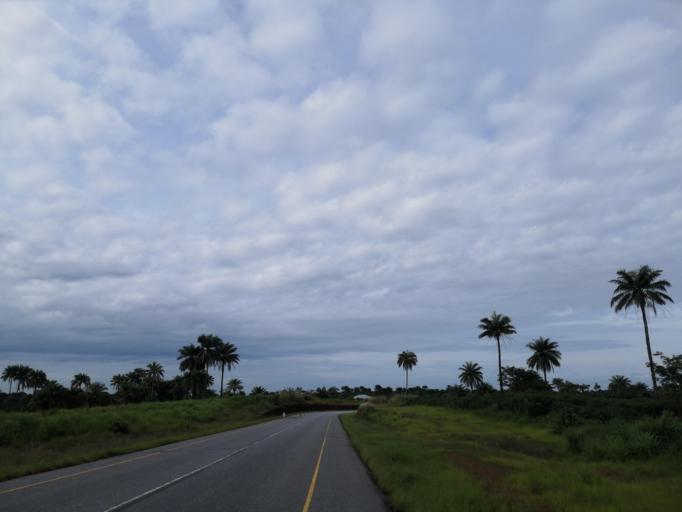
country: SL
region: Northern Province
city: Port Loko
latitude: 8.7887
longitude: -12.8481
